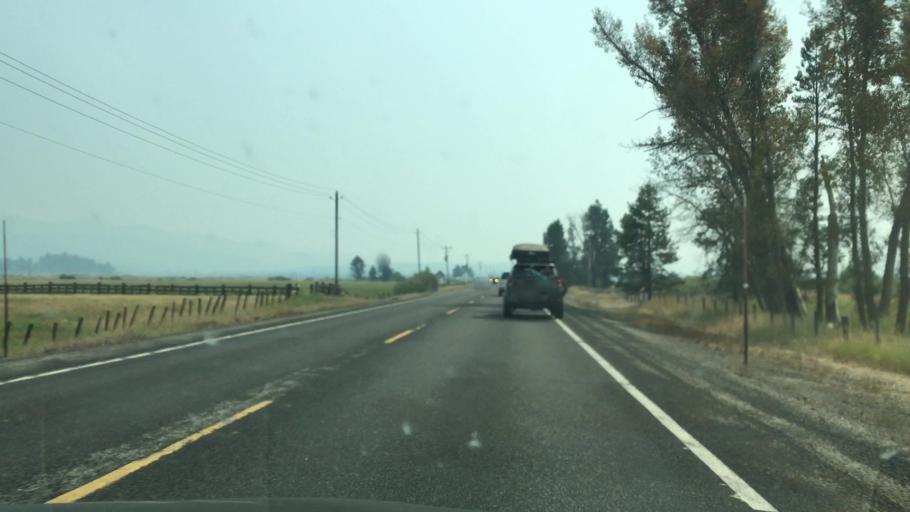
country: US
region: Idaho
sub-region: Valley County
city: Cascade
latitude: 44.4325
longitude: -115.9995
